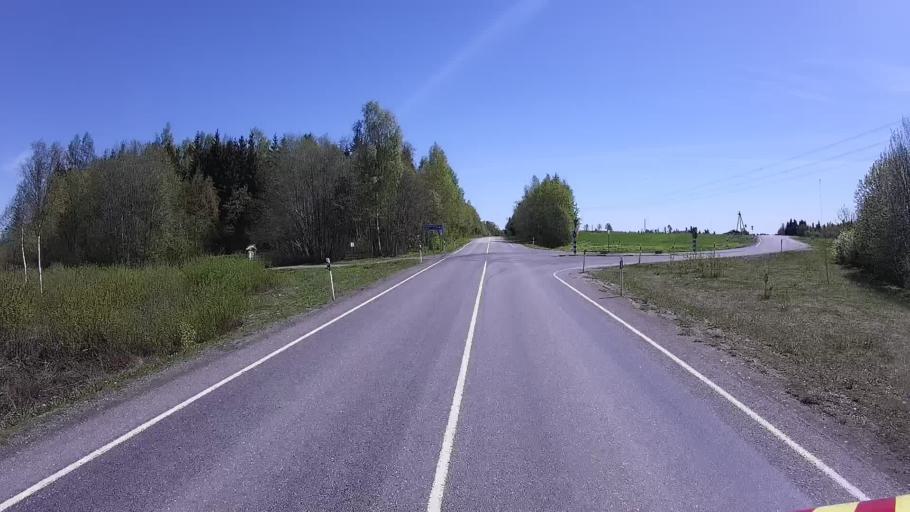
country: EE
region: Raplamaa
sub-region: Kehtna vald
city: Kehtna
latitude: 59.0432
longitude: 25.0305
